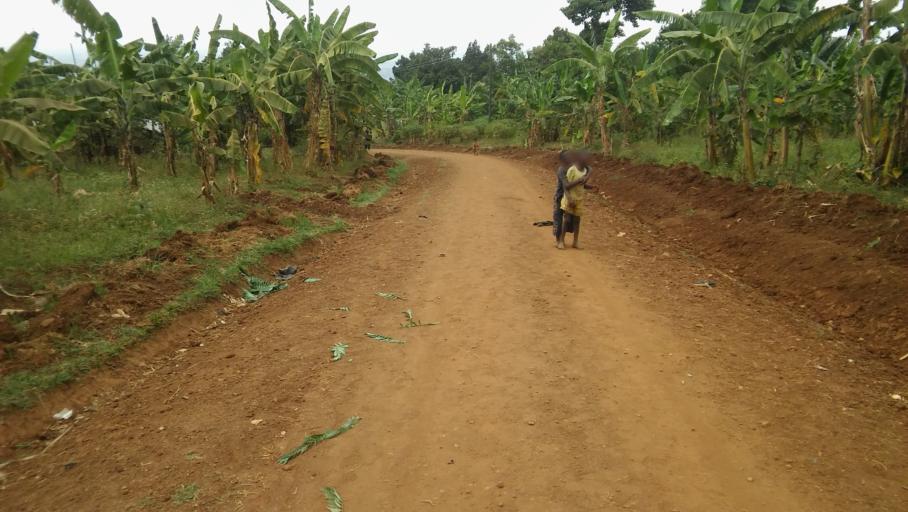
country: UG
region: Eastern Region
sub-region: Mbale District
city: Mbale
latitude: 1.0574
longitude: 34.2178
